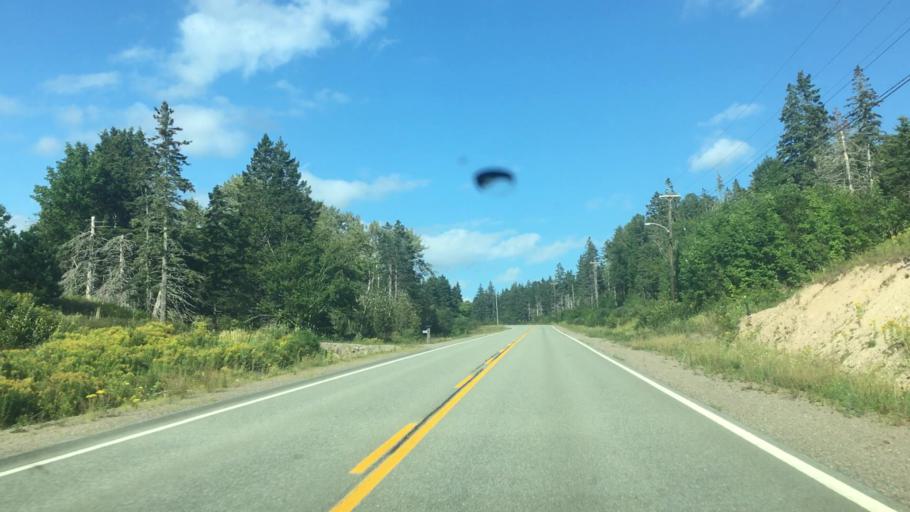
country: CA
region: Nova Scotia
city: Sydney
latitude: 45.8529
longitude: -60.6330
